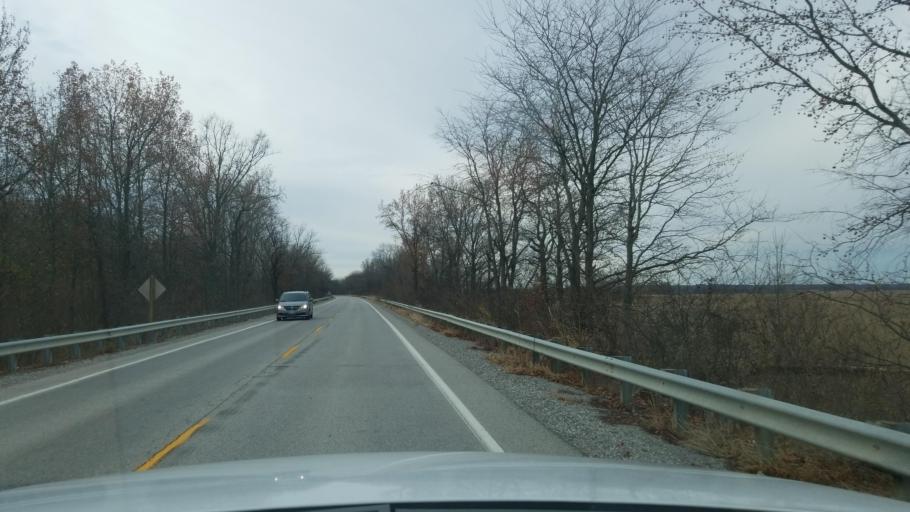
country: US
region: Illinois
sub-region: White County
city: Carmi
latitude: 37.9370
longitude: -88.0773
